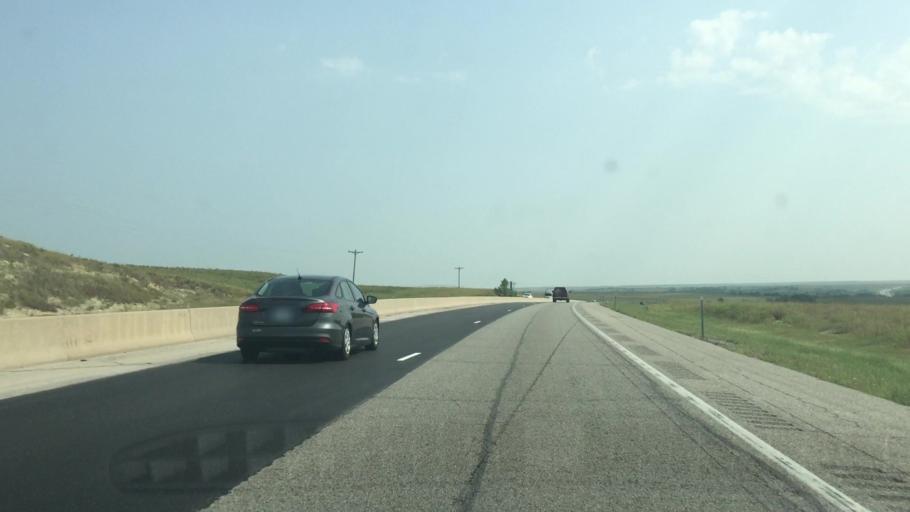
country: US
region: Kansas
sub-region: Chase County
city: Cottonwood Falls
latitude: 38.1129
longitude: -96.5714
